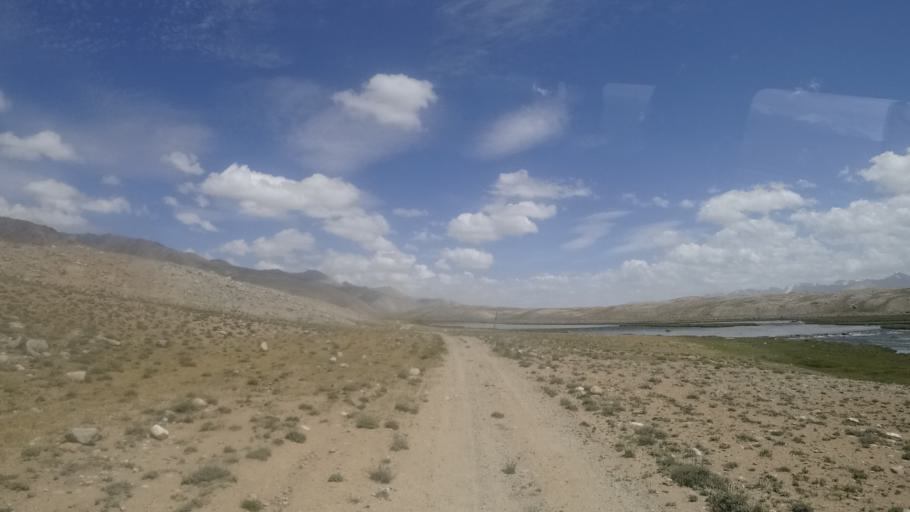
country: TJ
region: Gorno-Badakhshan
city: Murghob
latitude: 37.4678
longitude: 73.4185
